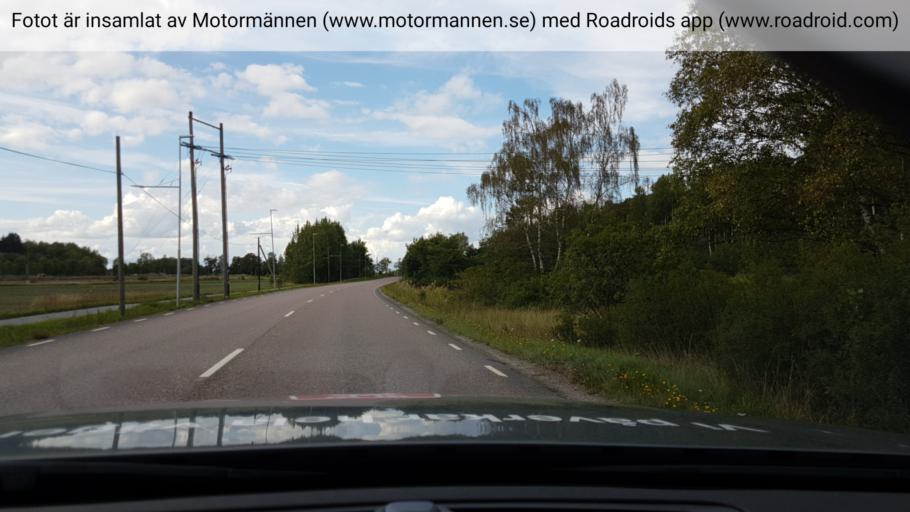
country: SE
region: Stockholm
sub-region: Upplands-Bro Kommun
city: Bro
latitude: 59.4972
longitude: 17.6758
